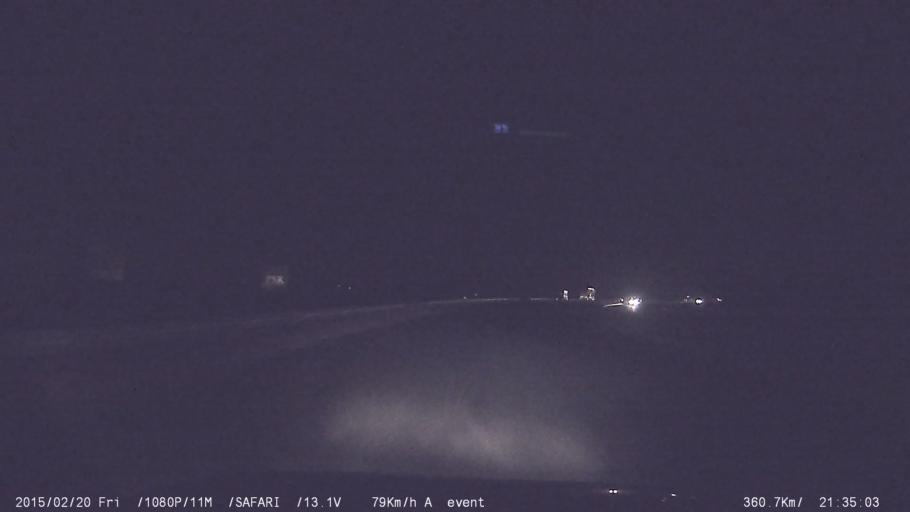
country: IN
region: Tamil Nadu
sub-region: Tiruppur
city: Avinashi
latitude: 11.1771
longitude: 77.2835
